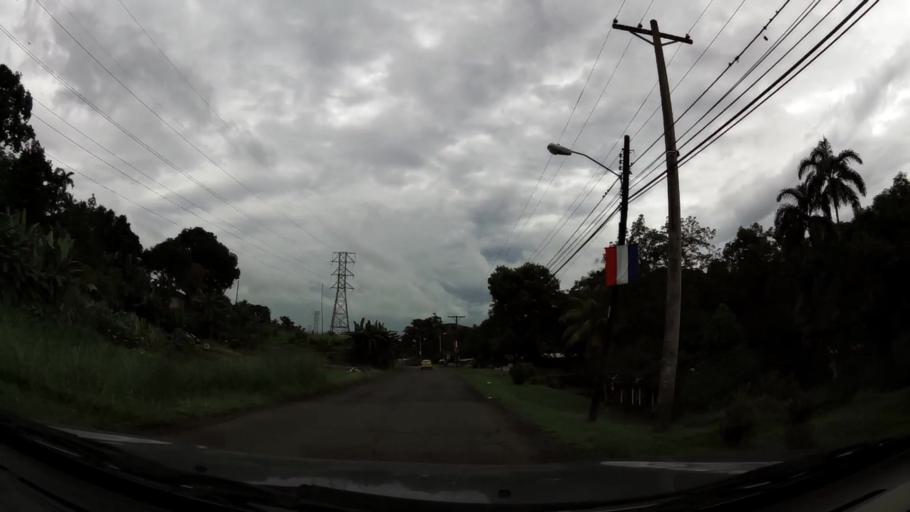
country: PA
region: Panama
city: Chilibre
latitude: 9.1689
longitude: -79.6120
